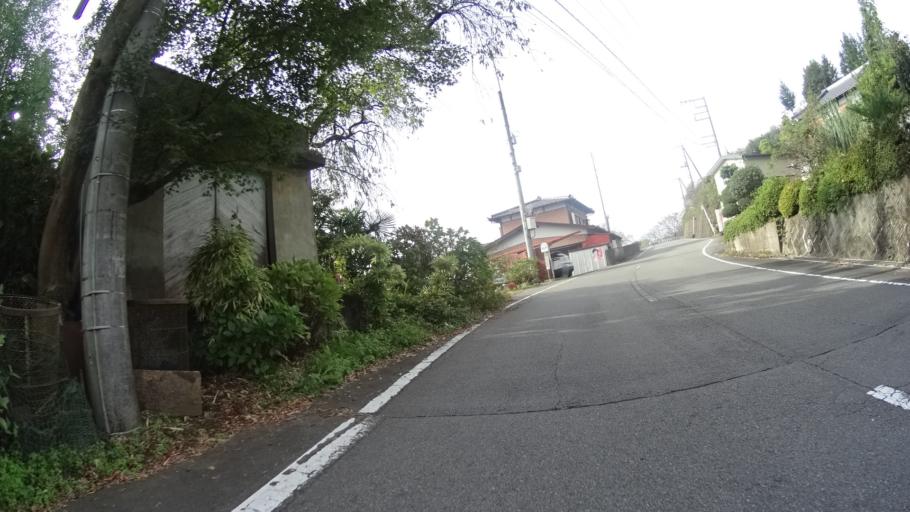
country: JP
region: Yamanashi
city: Uenohara
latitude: 35.6292
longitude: 139.0432
